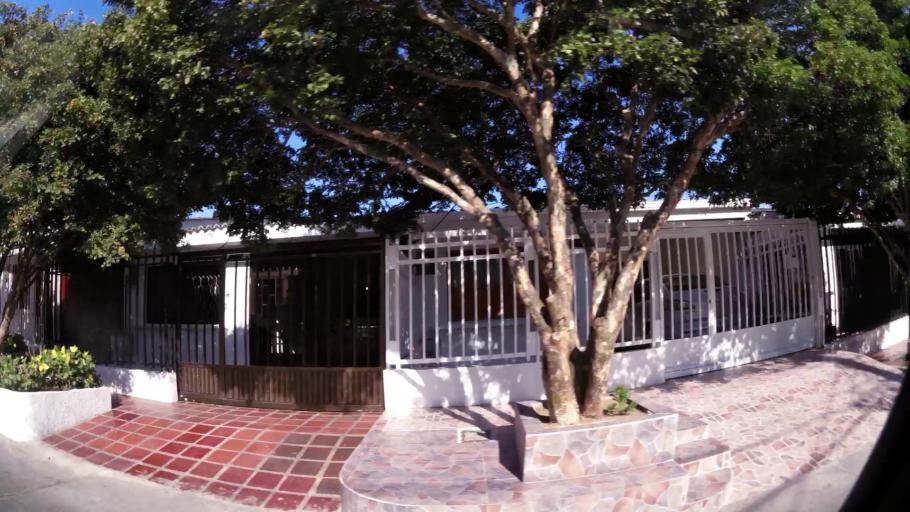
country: CO
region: Atlantico
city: Barranquilla
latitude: 11.0187
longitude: -74.8028
